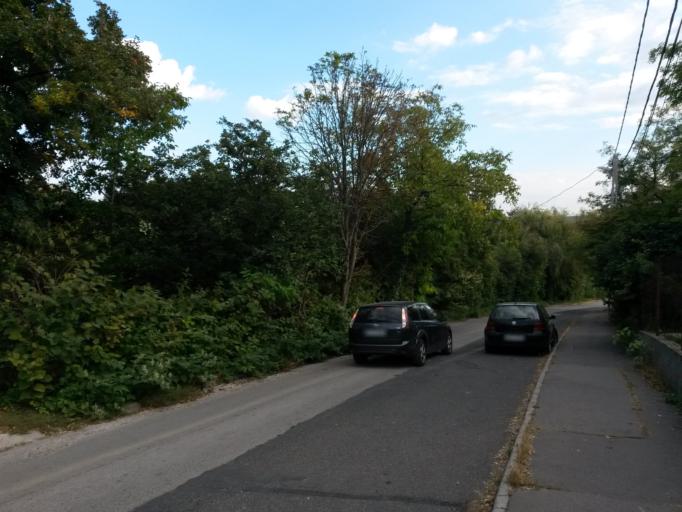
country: HU
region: Pest
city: Budaors
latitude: 47.4661
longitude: 18.9628
